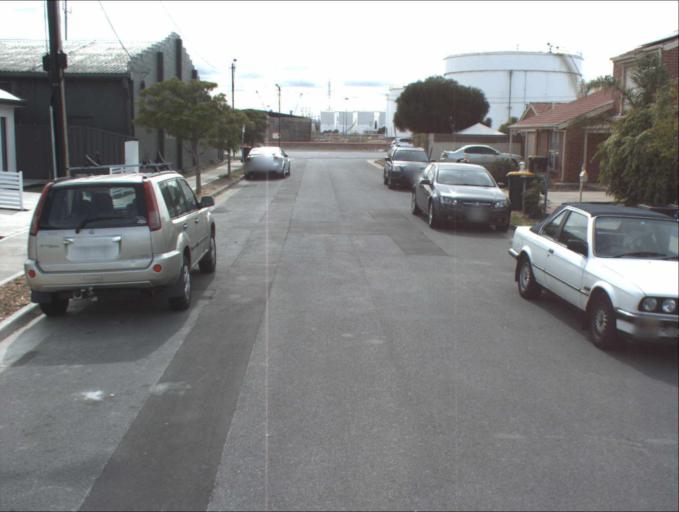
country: AU
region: South Australia
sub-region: Port Adelaide Enfield
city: Birkenhead
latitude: -34.8269
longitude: 138.4994
